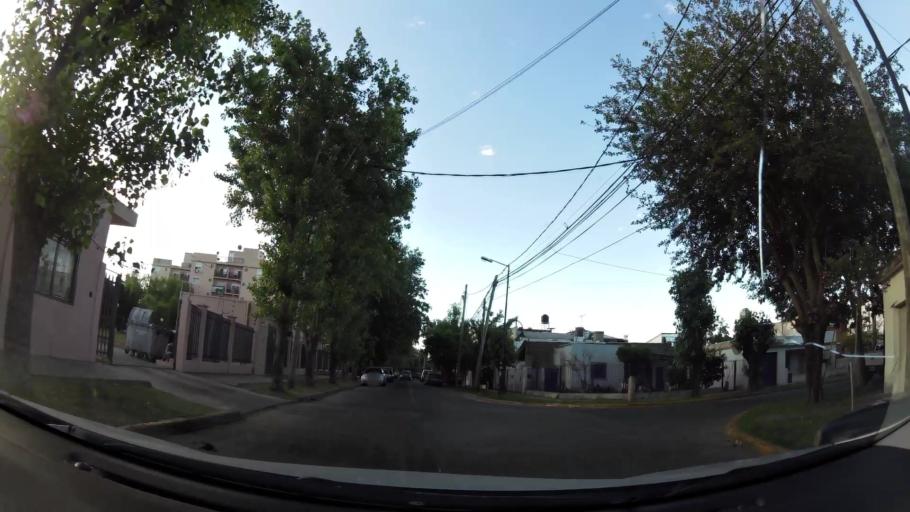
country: AR
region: Buenos Aires
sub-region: Partido de Tigre
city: Tigre
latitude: -34.4527
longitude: -58.5712
